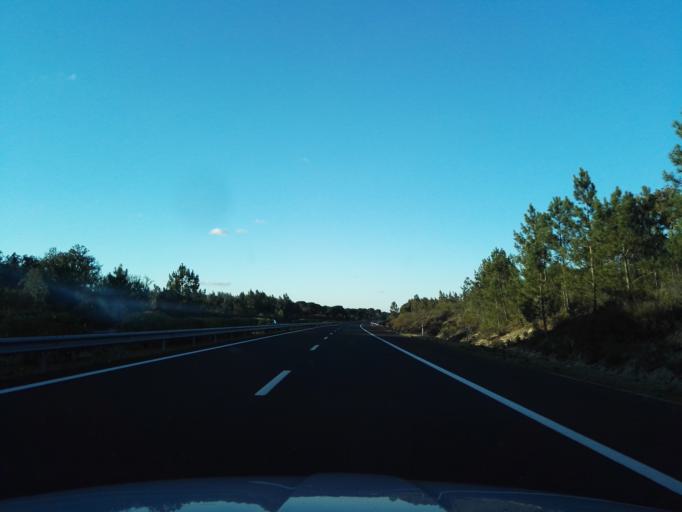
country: PT
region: Santarem
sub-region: Benavente
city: Poceirao
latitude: 38.7347
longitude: -8.6774
